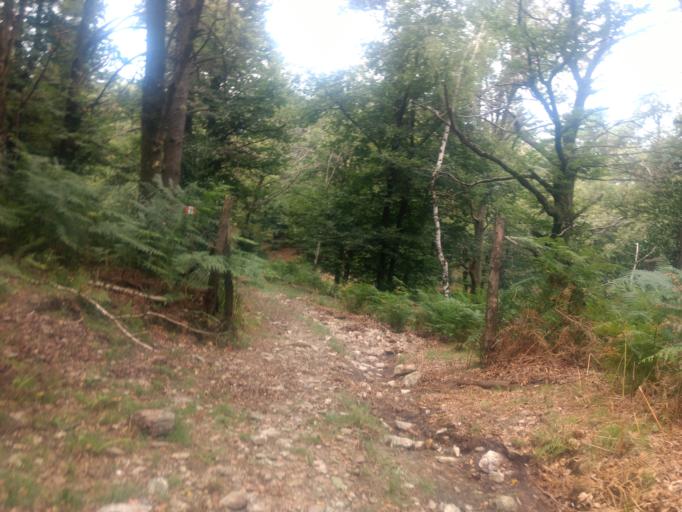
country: IT
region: Piedmont
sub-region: Provincia Verbano-Cusio-Ossola
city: Cambiasca
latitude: 45.9457
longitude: 8.5352
